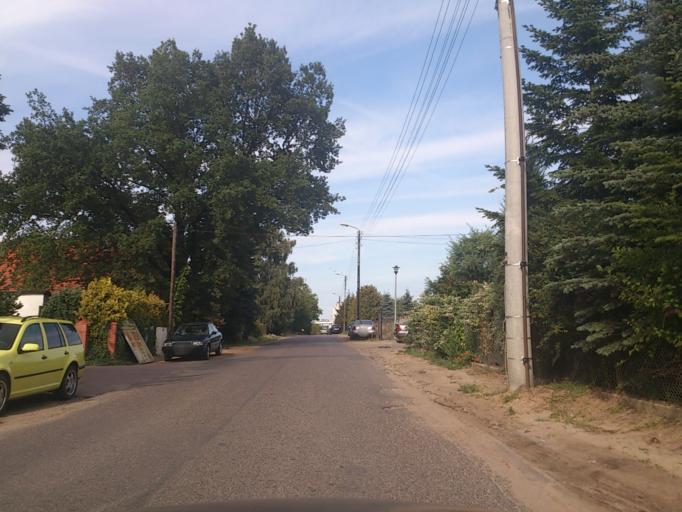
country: PL
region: Kujawsko-Pomorskie
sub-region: Powiat golubsko-dobrzynski
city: Golub-Dobrzyn
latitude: 53.1181
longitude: 19.0414
